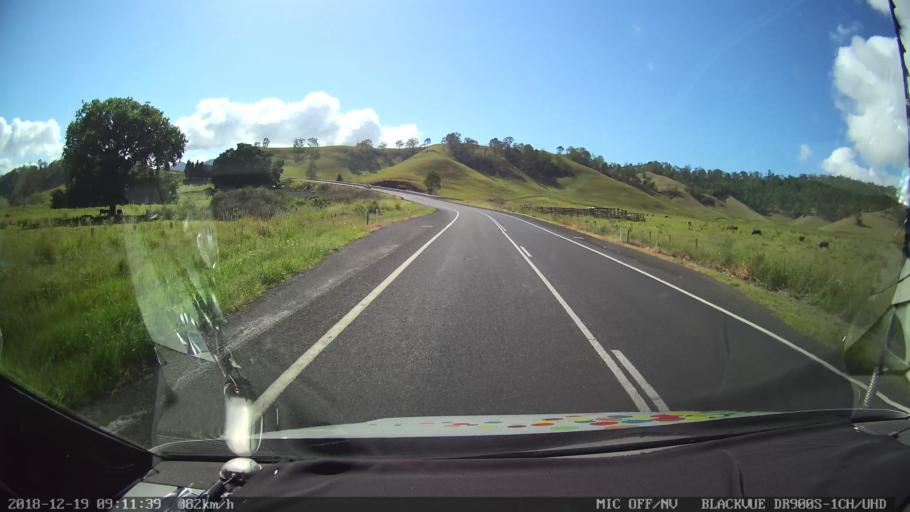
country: AU
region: New South Wales
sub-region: Kyogle
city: Kyogle
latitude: -28.4945
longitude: 152.9404
